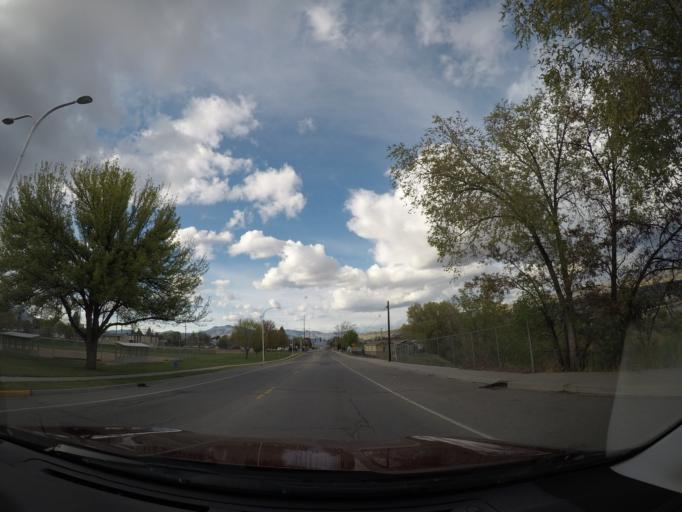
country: US
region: Washington
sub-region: Douglas County
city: East Wenatchee
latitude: 47.4029
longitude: -120.3030
